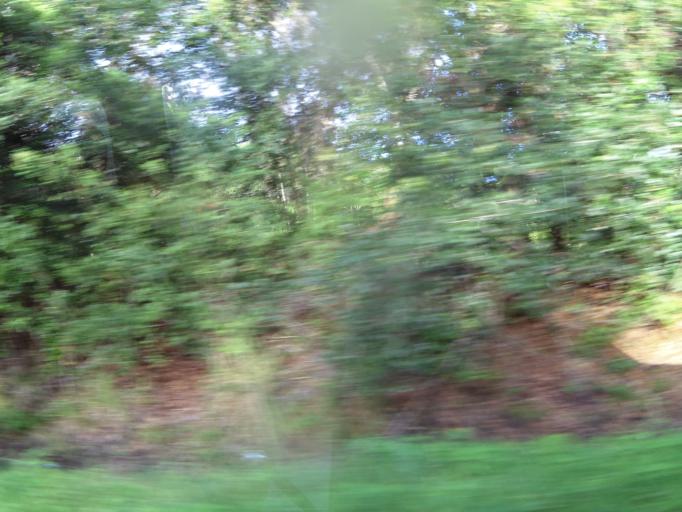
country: US
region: Florida
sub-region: Nassau County
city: Nassau Village-Ratliff
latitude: 30.3998
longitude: -81.7823
